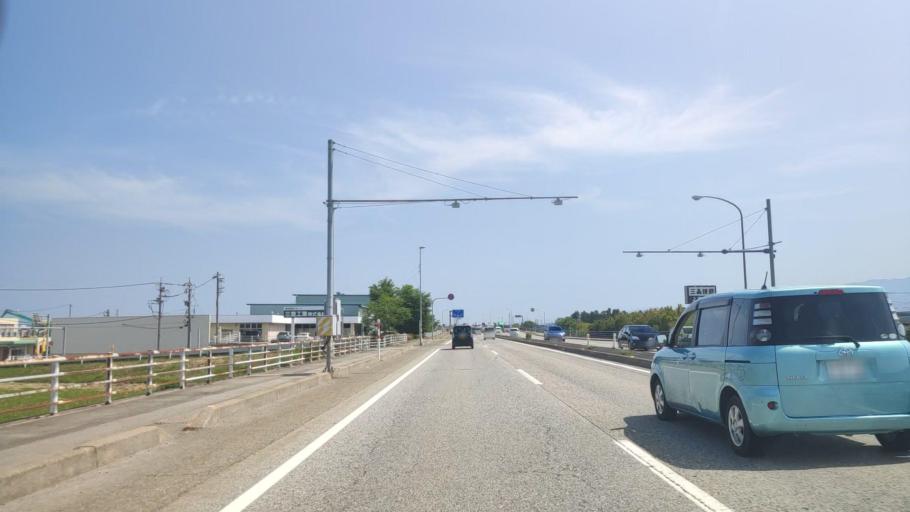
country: JP
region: Toyama
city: Namerikawa
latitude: 36.7369
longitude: 137.3385
